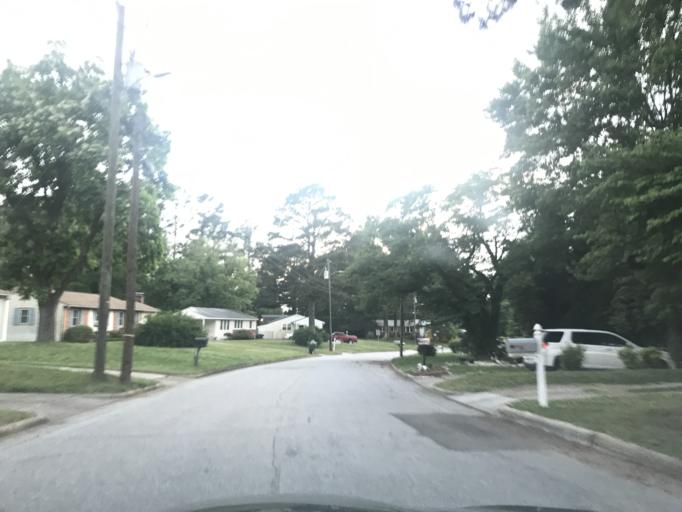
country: US
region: North Carolina
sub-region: Wake County
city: Raleigh
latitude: 35.8253
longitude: -78.6148
